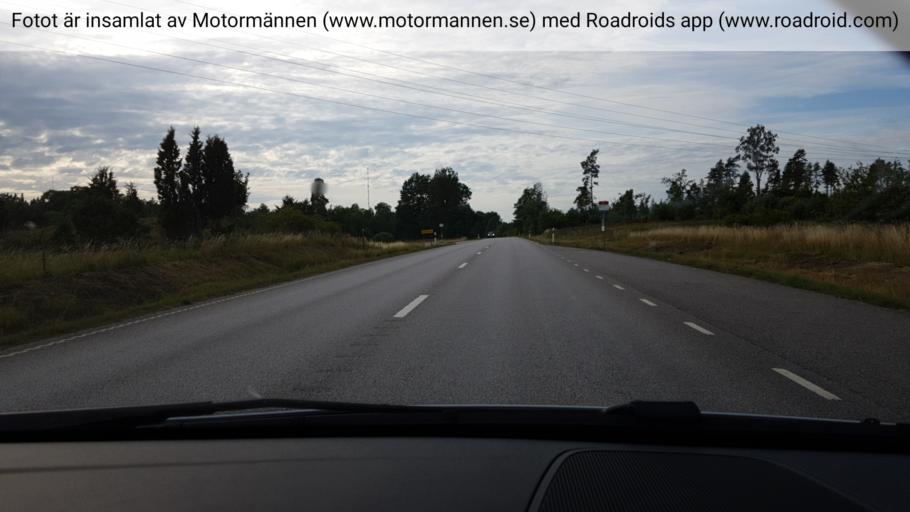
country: SE
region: Stockholm
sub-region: Norrtalje Kommun
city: Norrtalje
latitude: 59.8844
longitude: 18.6805
